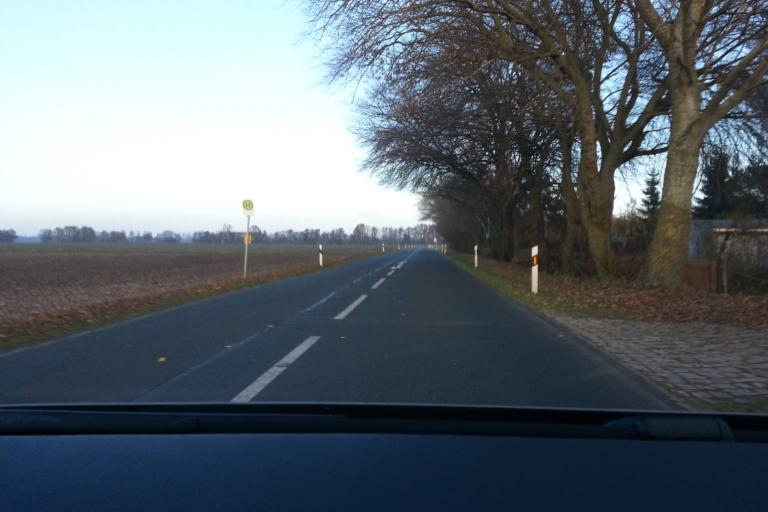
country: DE
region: Mecklenburg-Vorpommern
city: Ferdinandshof
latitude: 53.6248
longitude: 13.7948
